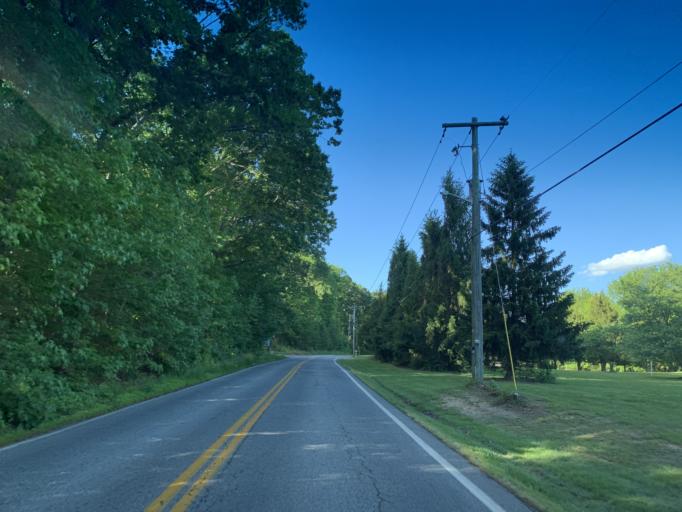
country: US
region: Maryland
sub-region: Cecil County
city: Elkton
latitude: 39.5802
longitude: -75.8778
